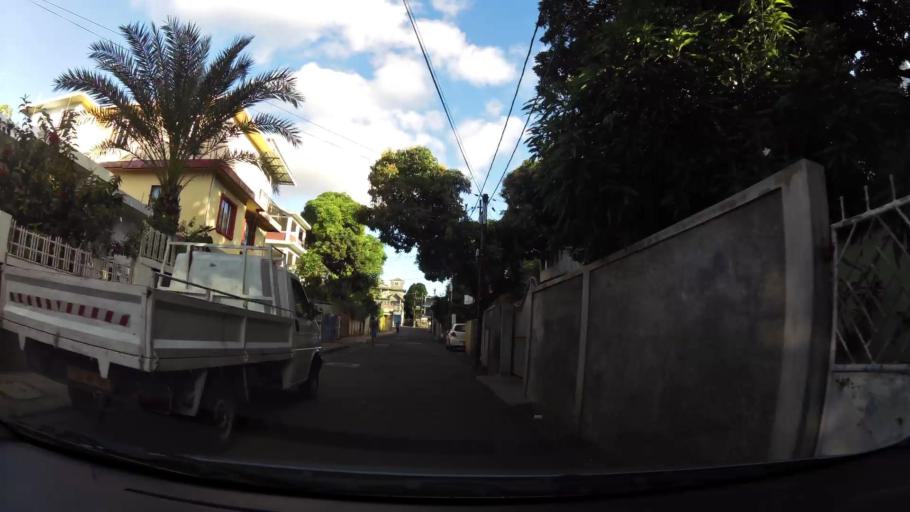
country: MU
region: Black River
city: Petite Riviere
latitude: -20.2204
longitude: 57.4641
